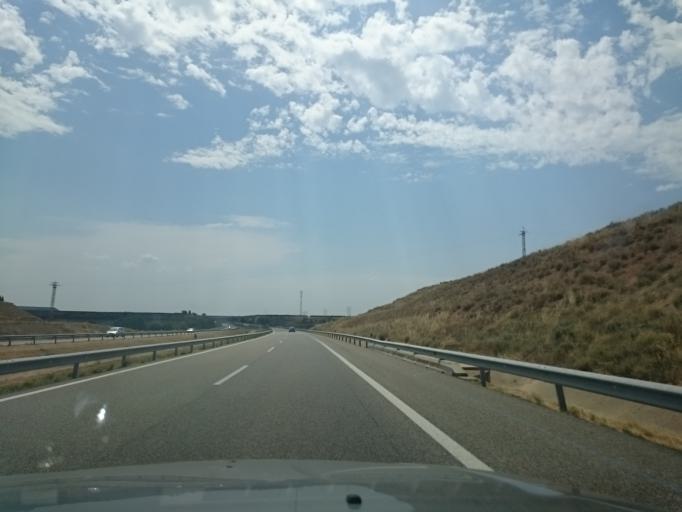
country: ES
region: Catalonia
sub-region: Provincia de Lleida
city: Sunyer
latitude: 41.5525
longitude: 0.5886
